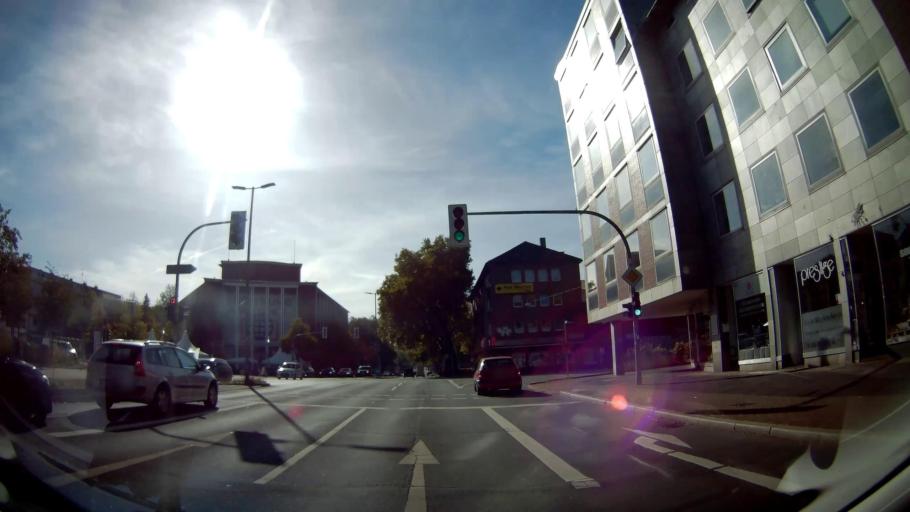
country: DE
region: North Rhine-Westphalia
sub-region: Regierungsbezirk Arnsberg
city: Bochum
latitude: 51.4735
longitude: 7.2162
